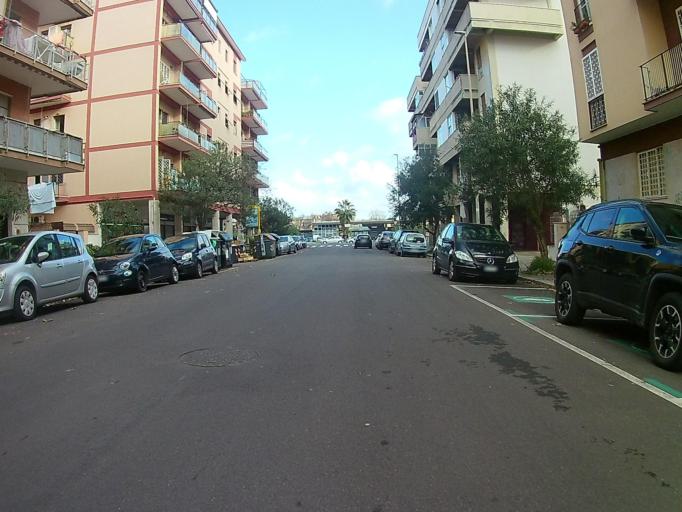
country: IT
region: Latium
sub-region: Citta metropolitana di Roma Capitale
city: Lido di Ostia
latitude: 41.7261
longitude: 12.2935
